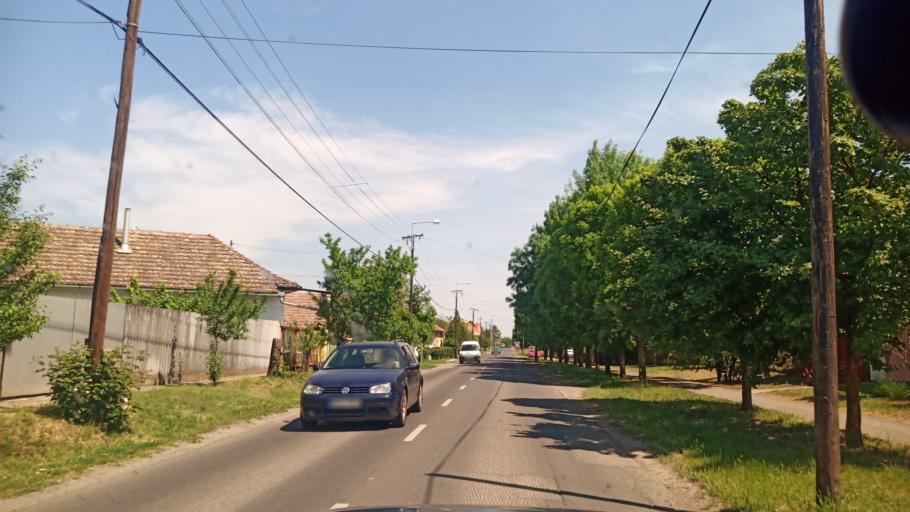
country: HU
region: Bekes
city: Oroshaza
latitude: 46.5617
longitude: 20.6167
